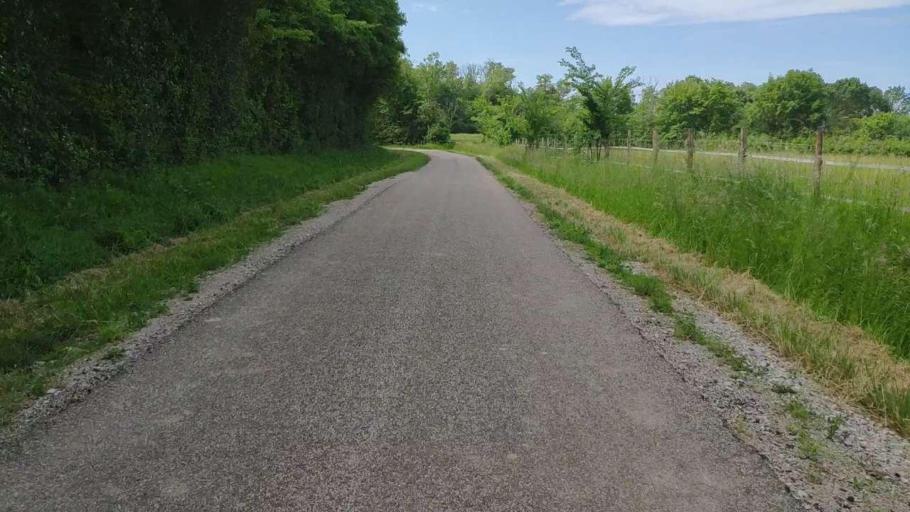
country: FR
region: Franche-Comte
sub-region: Departement du Jura
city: Bletterans
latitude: 46.6952
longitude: 5.4226
